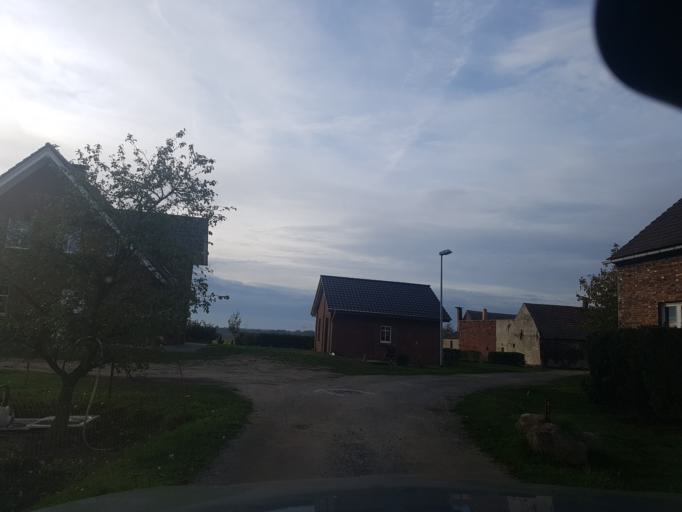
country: DE
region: Brandenburg
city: Doberlug-Kirchhain
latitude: 51.6130
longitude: 13.5859
